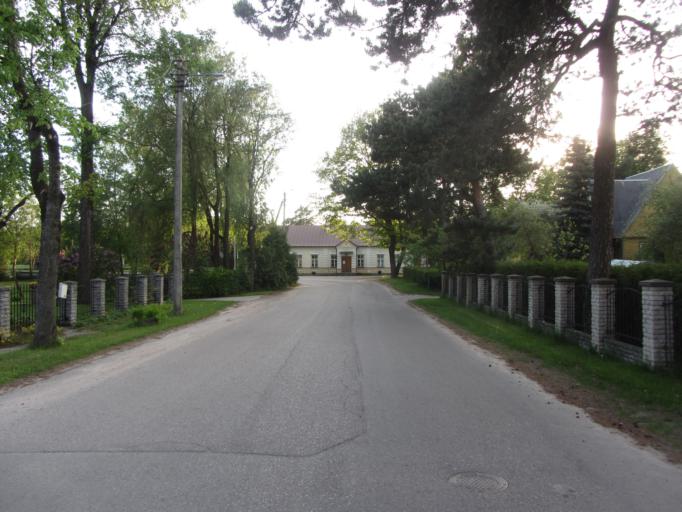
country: LT
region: Utenos apskritis
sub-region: Utena
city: Utena
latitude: 55.4941
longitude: 25.5836
